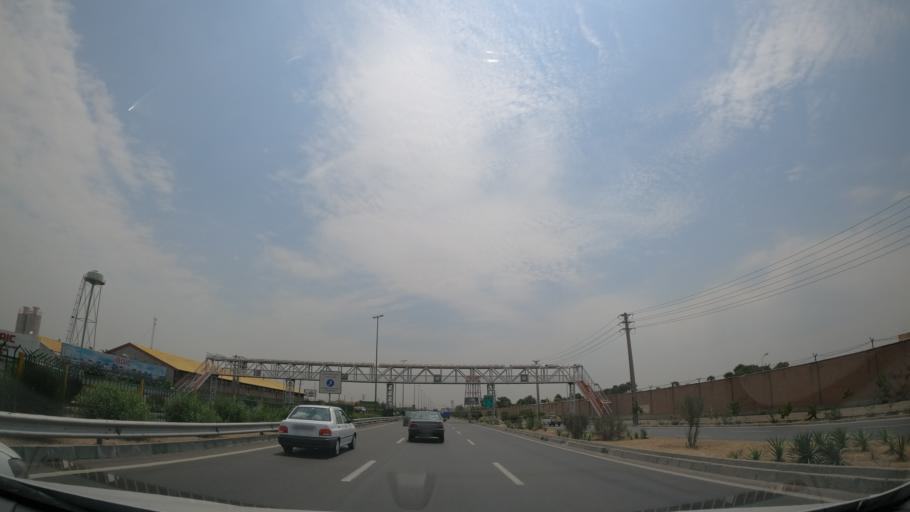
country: IR
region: Tehran
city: Shahr-e Qods
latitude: 35.6959
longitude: 51.2023
